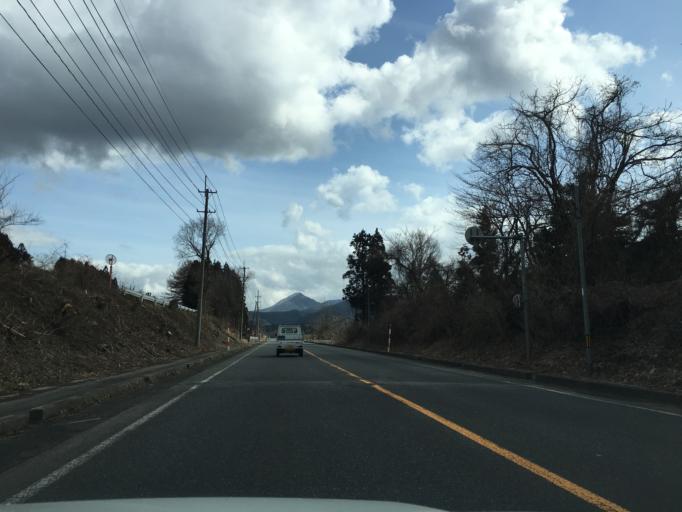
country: JP
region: Akita
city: Odate
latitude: 40.2206
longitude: 140.6086
